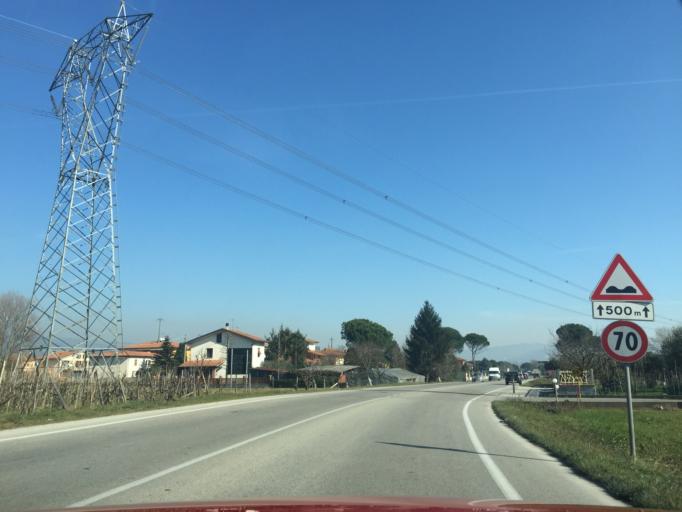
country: IT
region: Tuscany
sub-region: Provincia di Pistoia
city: Ponte Buggianese
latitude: 43.8515
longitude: 10.7421
